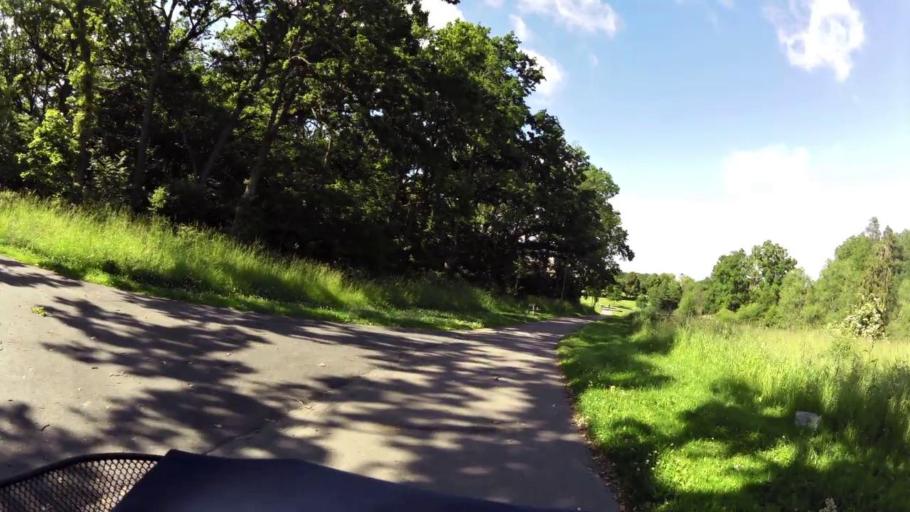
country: SE
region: OEstergoetland
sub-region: Linkopings Kommun
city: Linkoping
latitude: 58.3902
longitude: 15.6371
